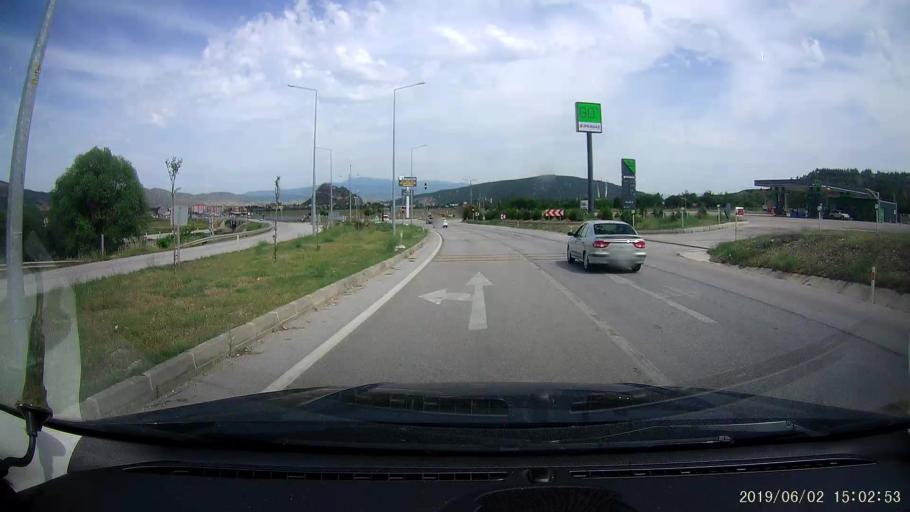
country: TR
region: Corum
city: Osmancik
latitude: 40.9779
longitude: 34.7728
